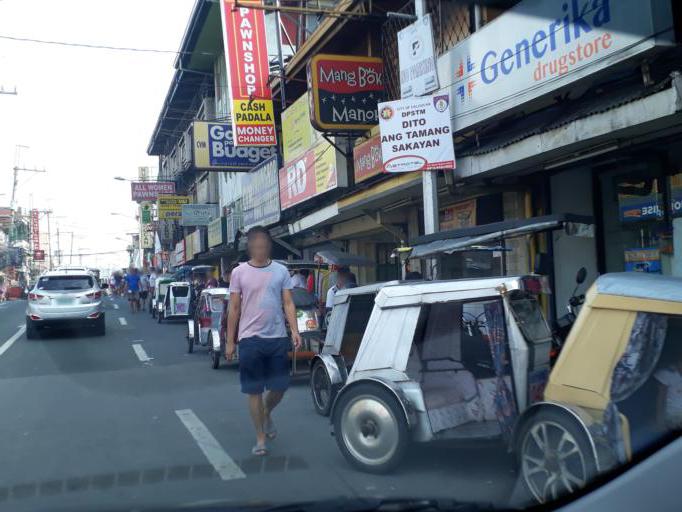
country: PH
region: Metro Manila
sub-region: Caloocan City
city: Niugan
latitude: 14.6378
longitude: 120.9756
